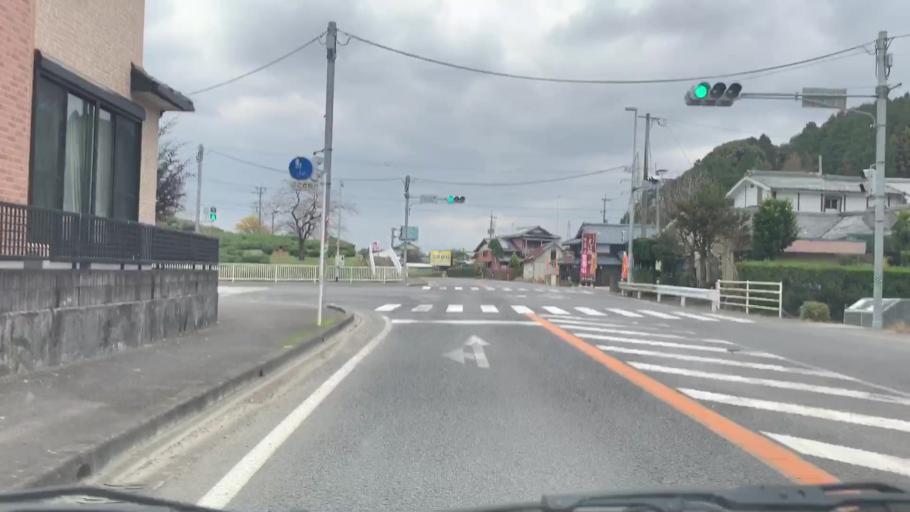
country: JP
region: Saga Prefecture
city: Ureshinomachi-shimojuku
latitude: 33.1363
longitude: 129.9880
